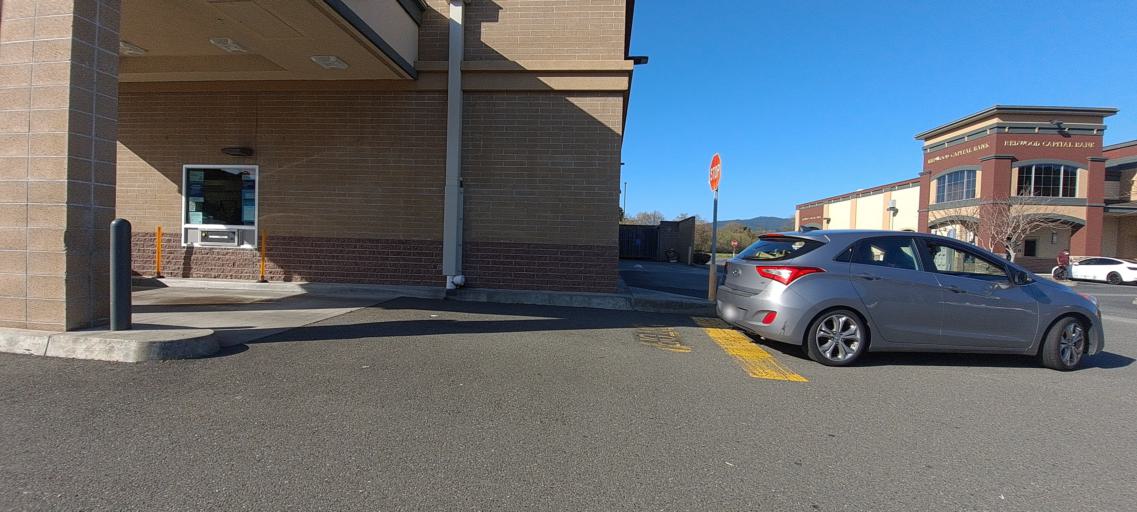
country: US
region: California
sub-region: Humboldt County
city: Fortuna
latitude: 40.5792
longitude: -124.1458
